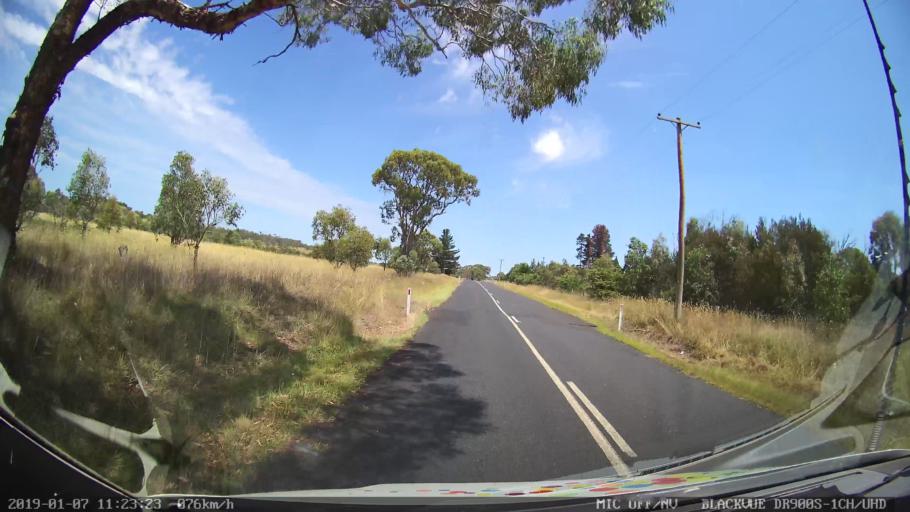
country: AU
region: New South Wales
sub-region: Armidale Dumaresq
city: Armidale
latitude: -30.4754
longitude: 151.6217
